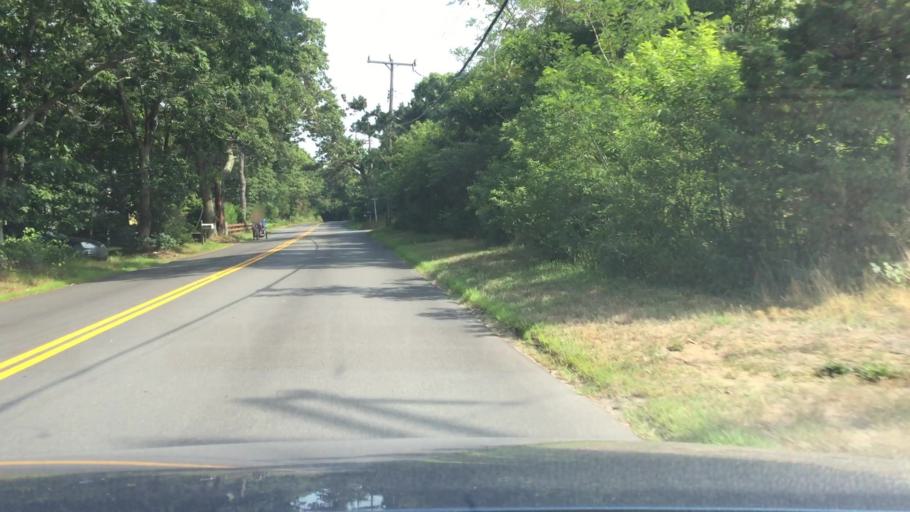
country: US
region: Massachusetts
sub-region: Barnstable County
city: North Eastham
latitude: 41.8636
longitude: -69.9815
